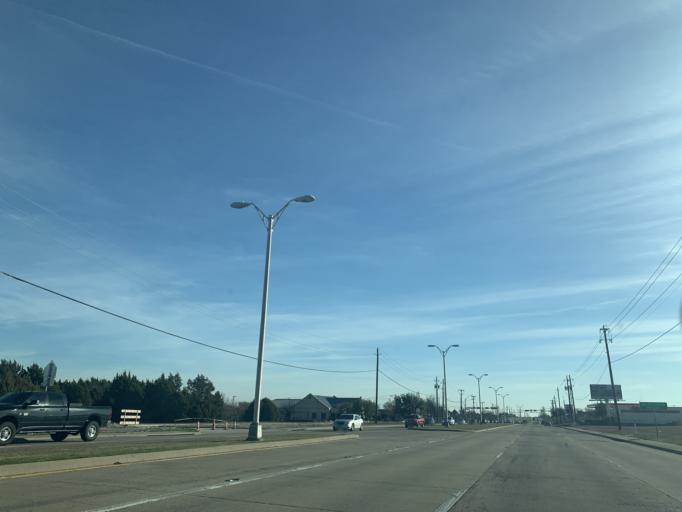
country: US
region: Texas
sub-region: Dallas County
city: Cedar Hill
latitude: 32.5898
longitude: -96.9281
